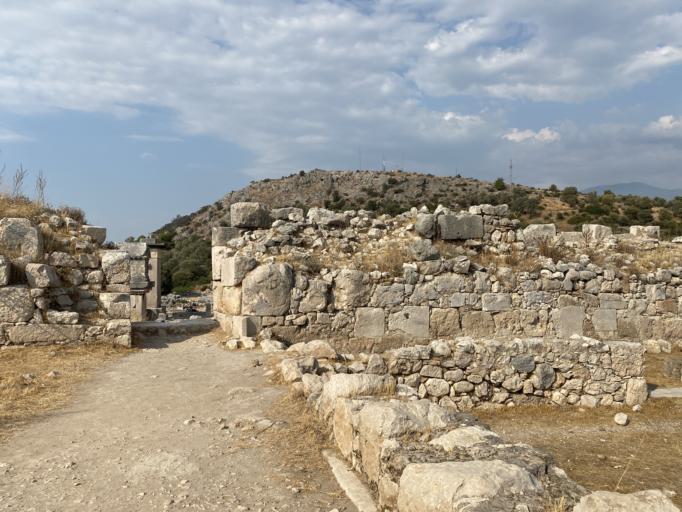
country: TR
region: Mugla
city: Esen
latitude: 36.3563
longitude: 29.3179
